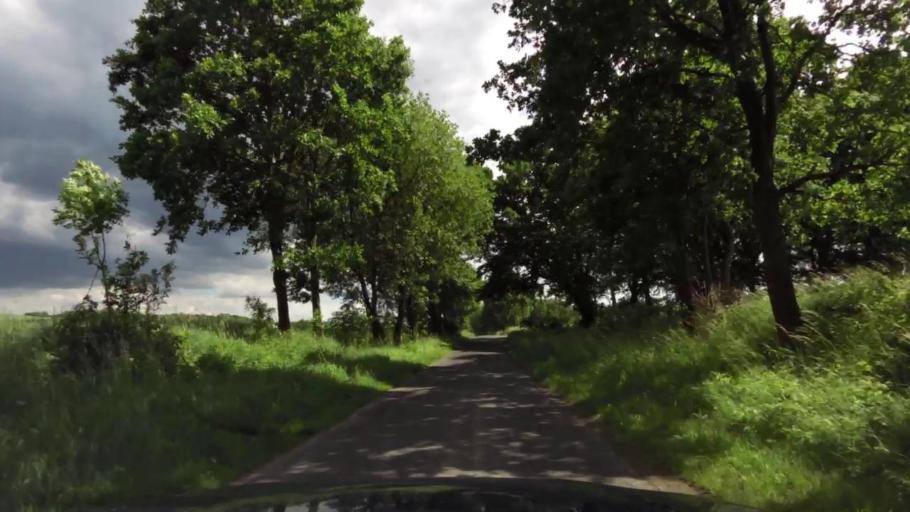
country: PL
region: West Pomeranian Voivodeship
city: Trzcinsko Zdroj
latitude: 52.9035
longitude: 14.6063
